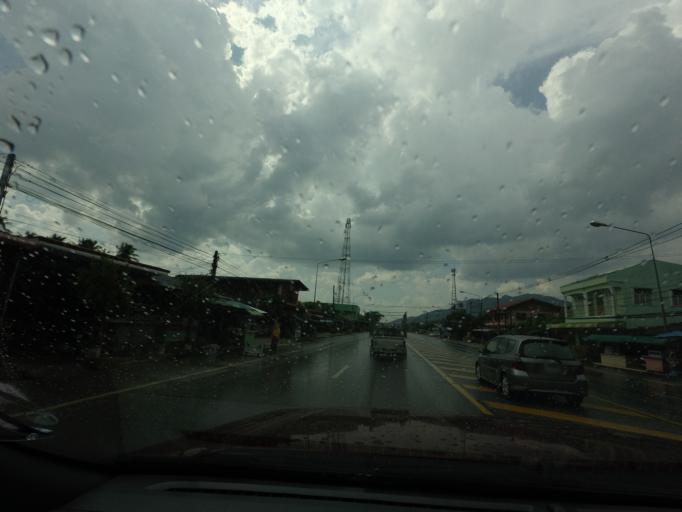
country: TH
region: Yala
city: Krong Pi Nang
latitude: 6.4196
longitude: 101.2789
